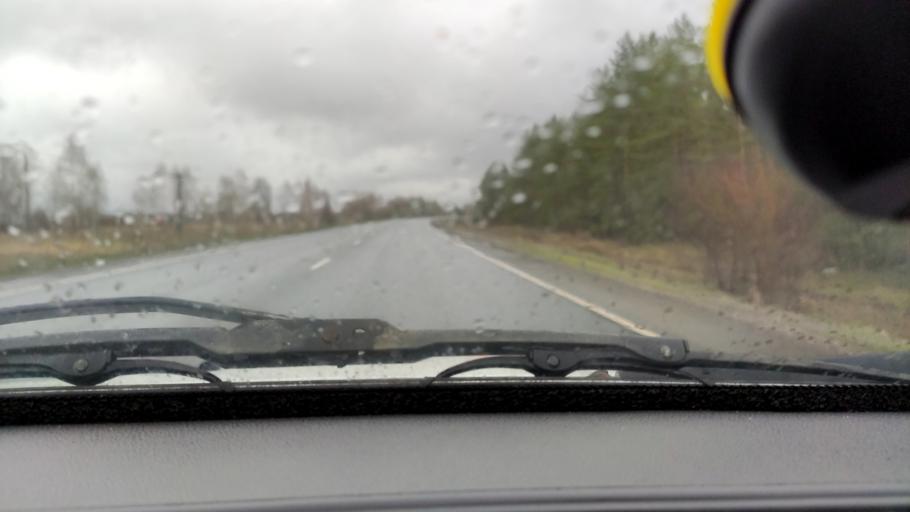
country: RU
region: Samara
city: Povolzhskiy
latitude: 53.5998
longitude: 49.5933
